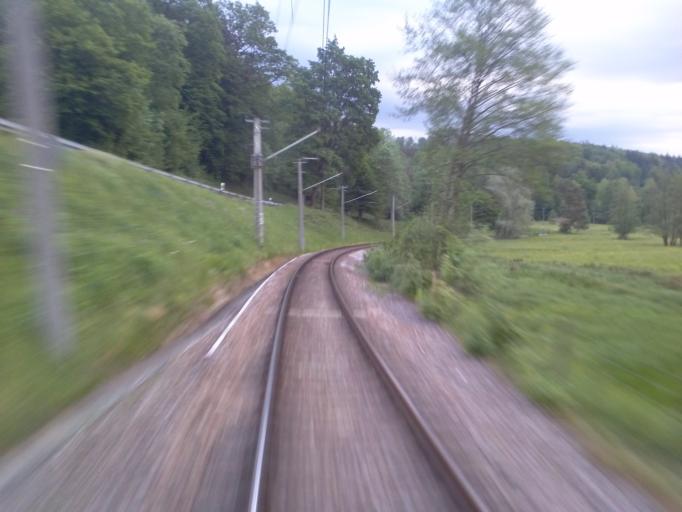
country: DE
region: Baden-Wuerttemberg
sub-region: Karlsruhe Region
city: Ettlingen
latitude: 48.8807
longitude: 8.4535
